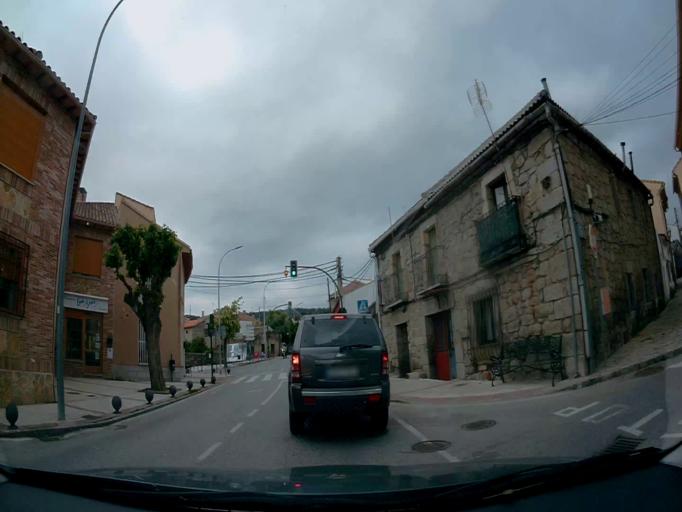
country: ES
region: Madrid
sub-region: Provincia de Madrid
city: Navalagamella
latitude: 40.4686
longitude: -4.1218
